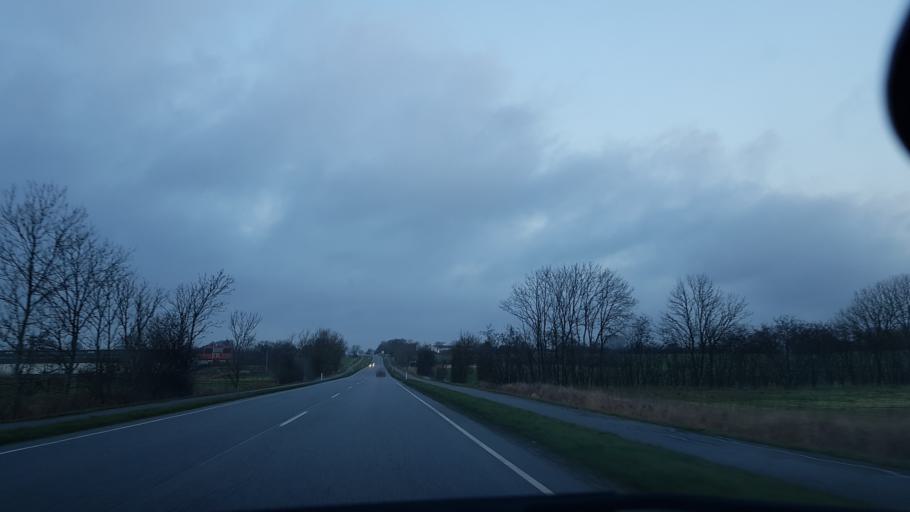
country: DK
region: South Denmark
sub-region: Haderslev Kommune
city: Haderslev
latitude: 55.2996
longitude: 9.4995
